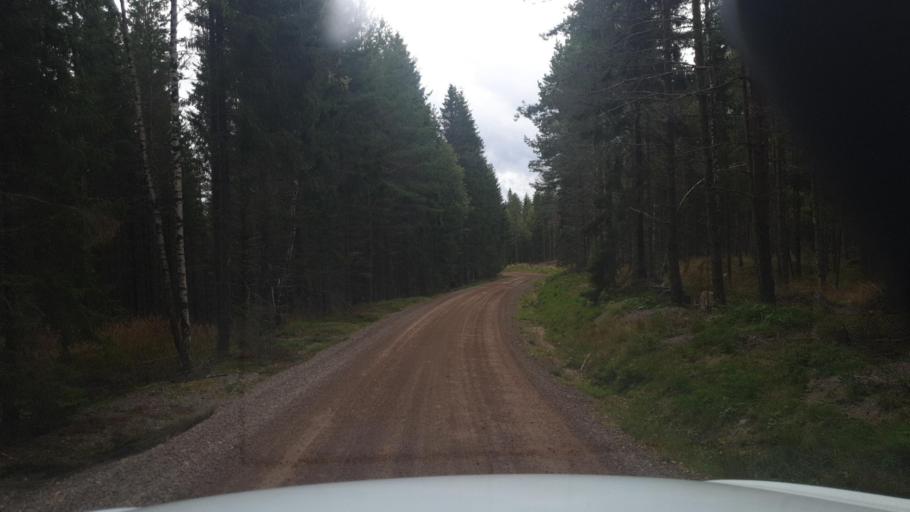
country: SE
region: Vaermland
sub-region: Arvika Kommun
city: Arvika
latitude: 59.9681
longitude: 12.6602
